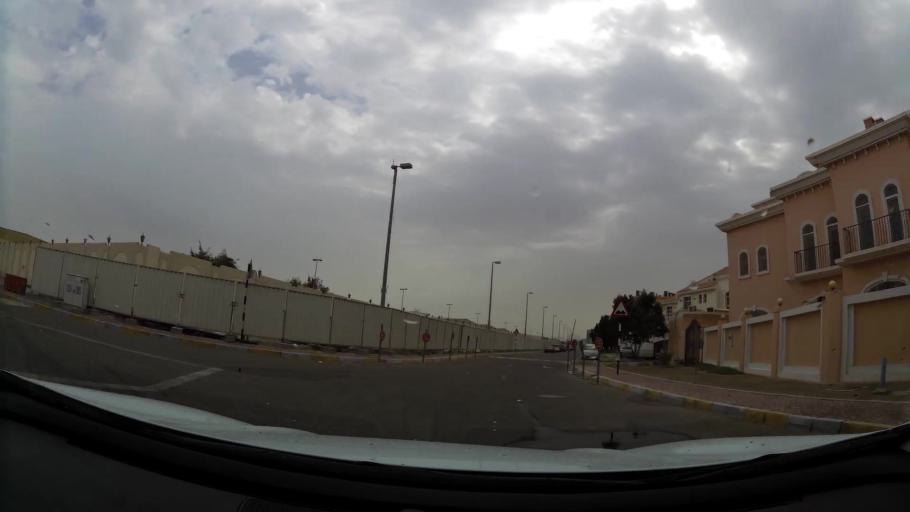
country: AE
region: Abu Dhabi
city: Abu Dhabi
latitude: 24.4330
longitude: 54.4437
